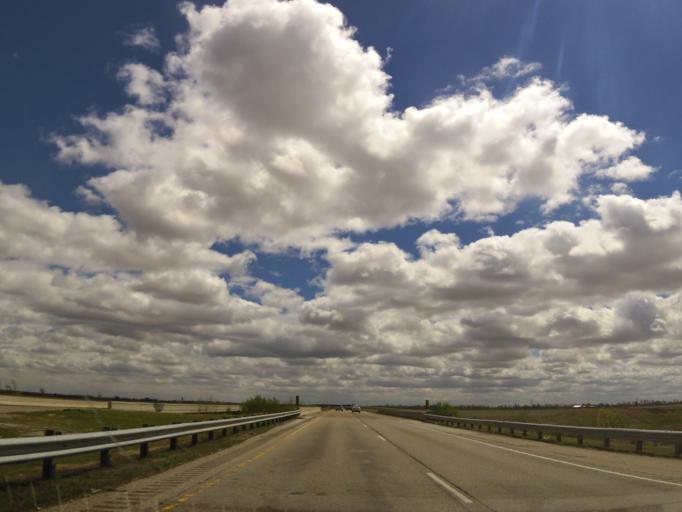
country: US
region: Arkansas
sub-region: Craighead County
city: Bay
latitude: 35.7125
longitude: -90.5753
